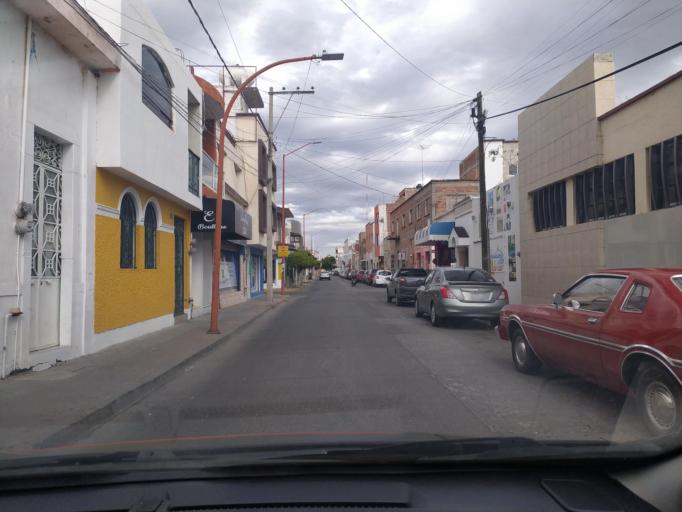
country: LA
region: Oudomxai
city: Muang La
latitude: 21.0198
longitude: 101.8601
